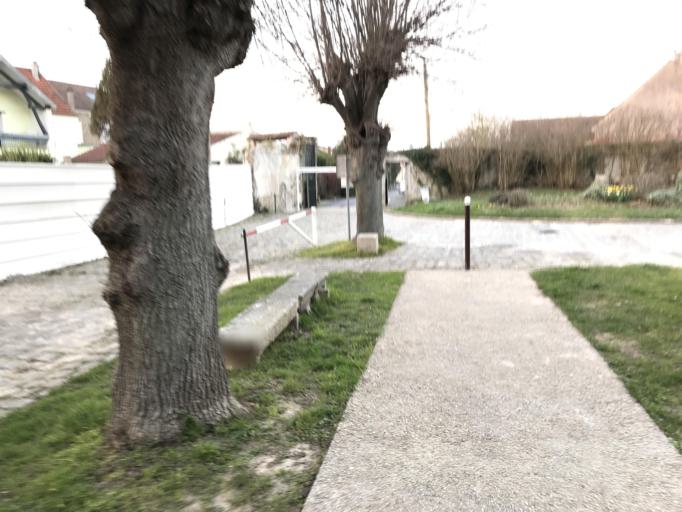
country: FR
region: Ile-de-France
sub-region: Departement de l'Essonne
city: Ballainvilliers
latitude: 48.6729
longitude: 2.2941
